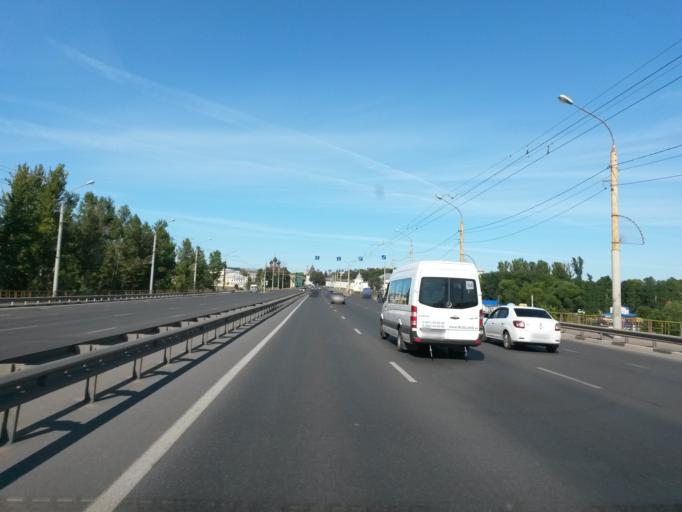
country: RU
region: Jaroslavl
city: Yaroslavl
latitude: 57.6162
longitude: 39.8846
